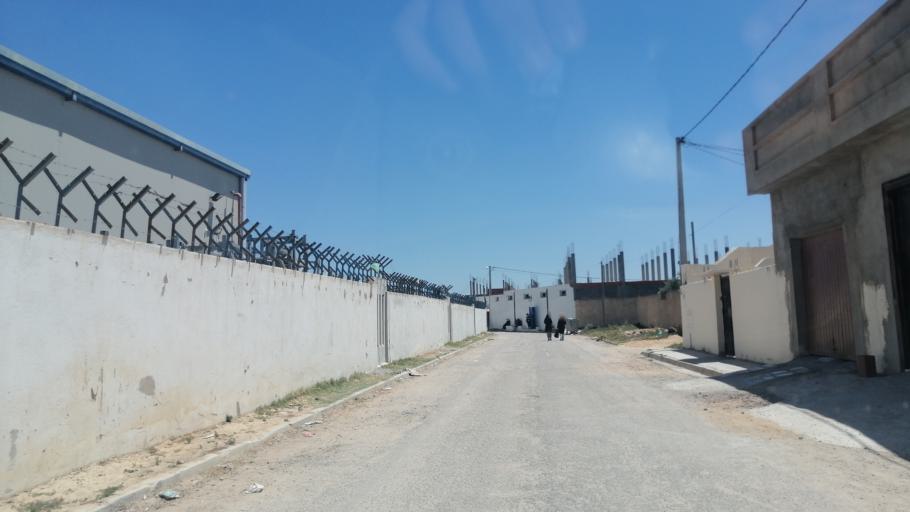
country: TN
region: Al Qayrawan
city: Sbikha
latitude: 36.1218
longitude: 10.0960
